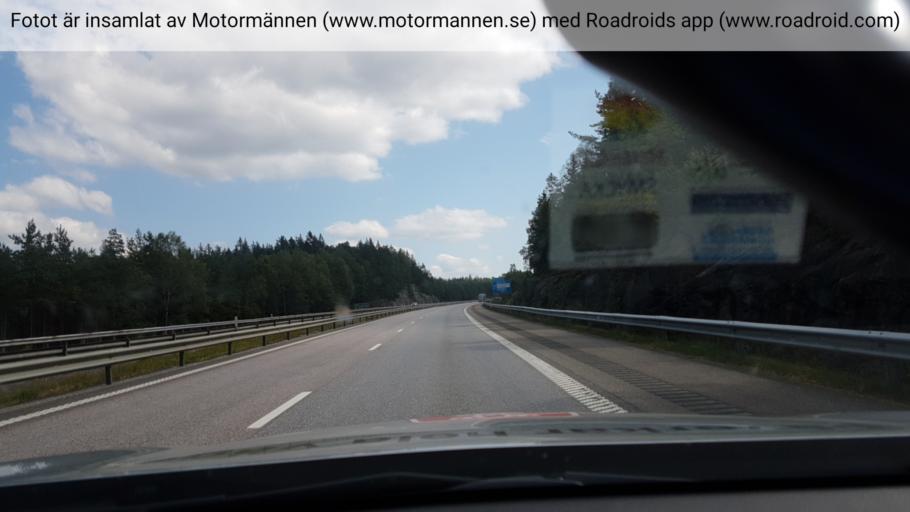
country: SE
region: Vaestra Goetaland
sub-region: Harryda Kommun
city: Landvetter
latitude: 57.6856
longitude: 12.2925
